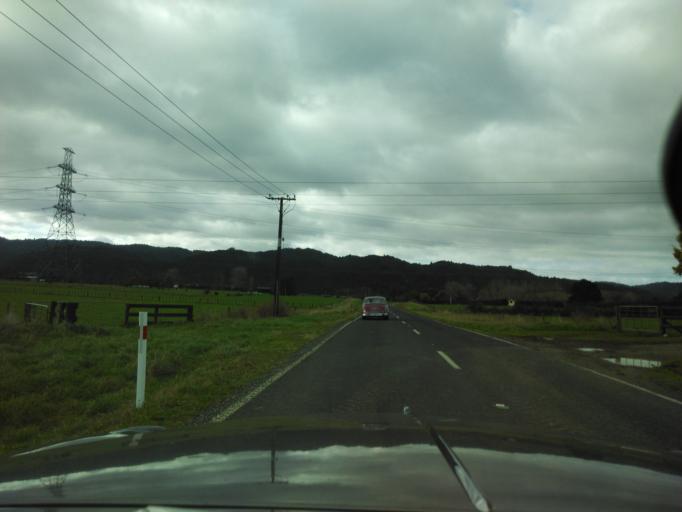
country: NZ
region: Auckland
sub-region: Auckland
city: Red Hill
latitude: -37.1097
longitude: 175.0849
